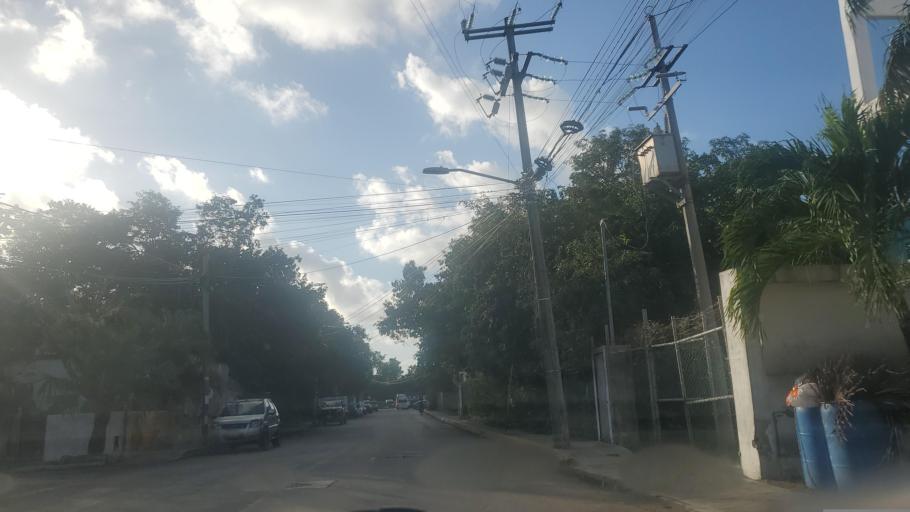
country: MX
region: Quintana Roo
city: Tulum
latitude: 20.2166
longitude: -87.4512
